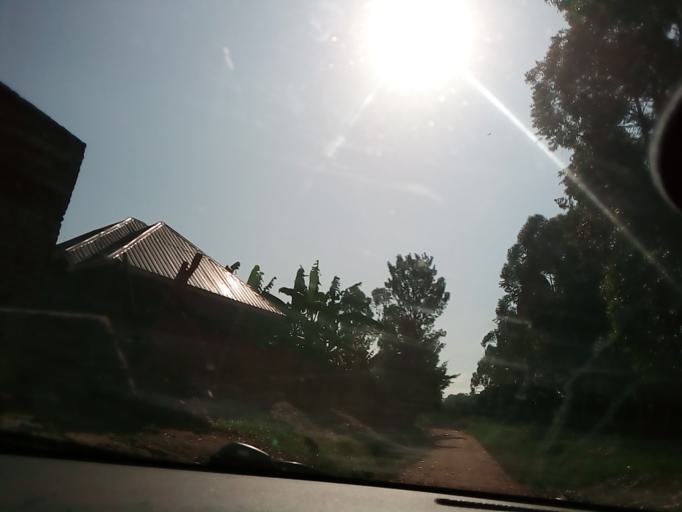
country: UG
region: Central Region
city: Masaka
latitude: -0.3393
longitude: 31.7260
